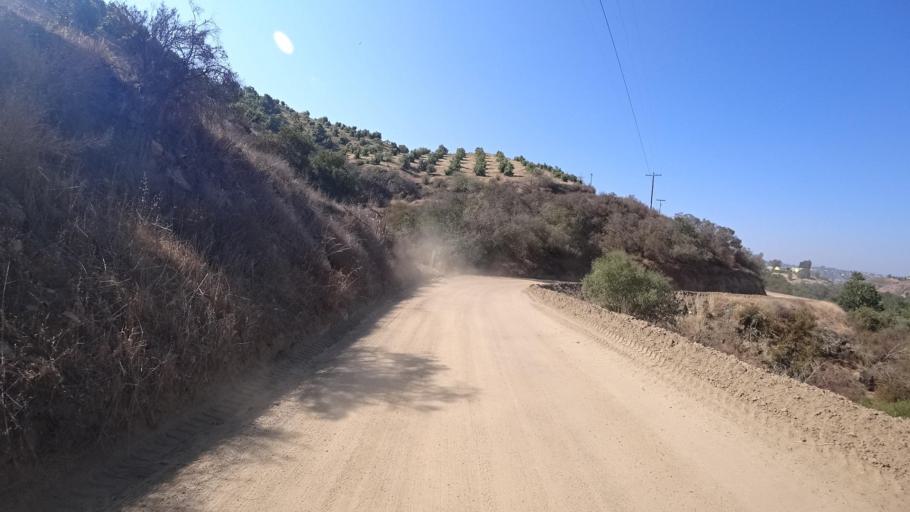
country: US
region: California
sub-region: San Diego County
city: Rainbow
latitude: 33.4201
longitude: -117.2048
